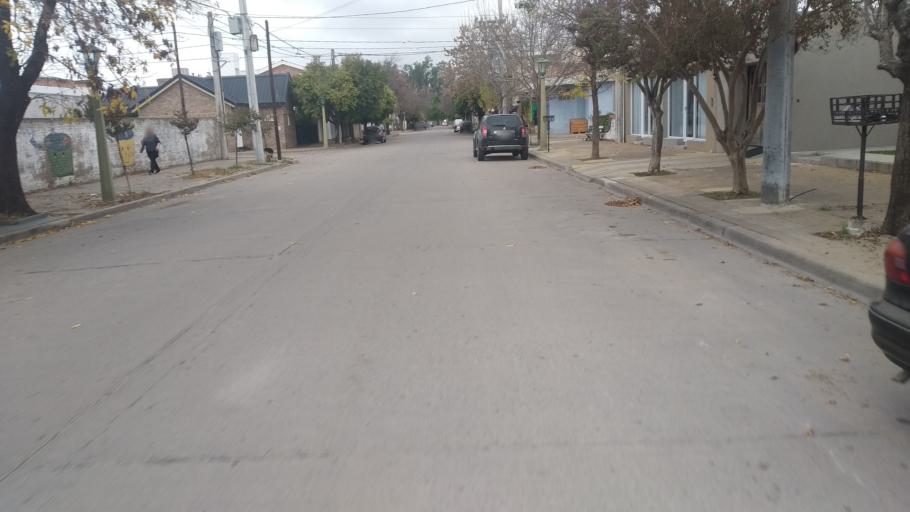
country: AR
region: Cordoba
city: Leones
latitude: -32.6611
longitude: -62.2998
